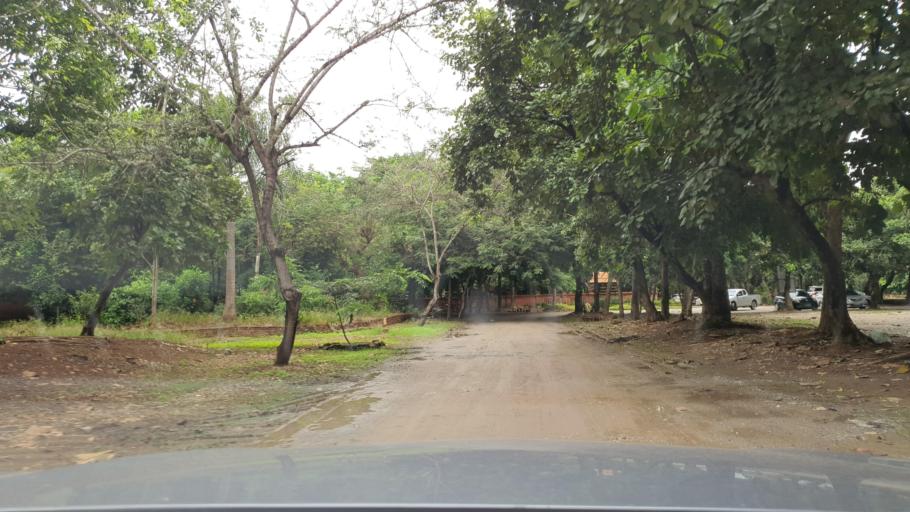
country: TH
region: Lamphun
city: Lamphun
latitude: 18.6039
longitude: 98.9747
